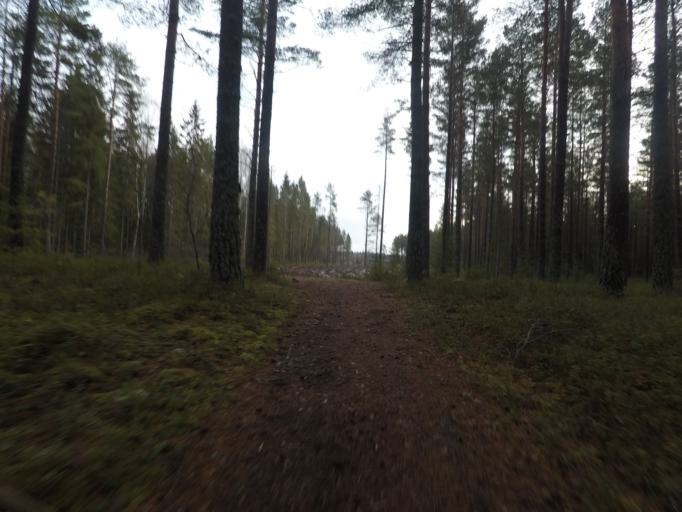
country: SE
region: Vaestmanland
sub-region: Kungsors Kommun
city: Kungsoer
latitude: 59.3464
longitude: 16.1163
